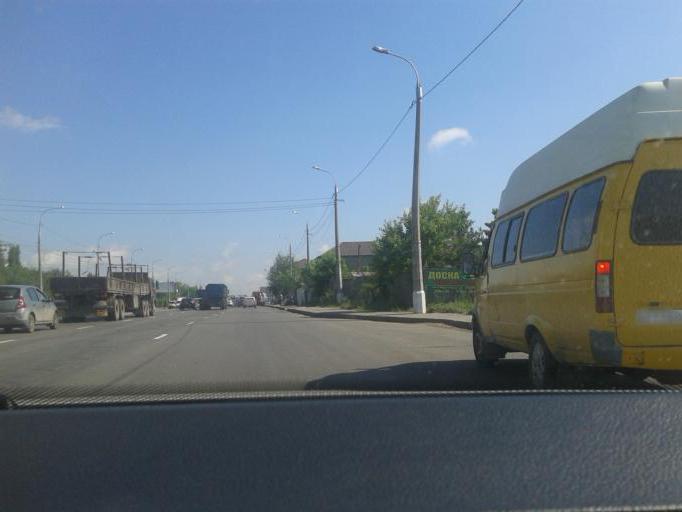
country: RU
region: Volgograd
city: Volgograd
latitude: 48.6711
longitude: 44.4426
